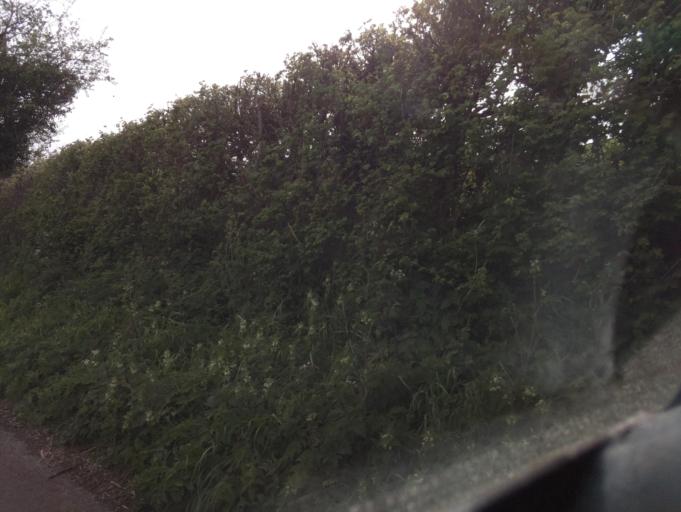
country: GB
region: England
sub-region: Somerset
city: Milborne Port
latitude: 50.9733
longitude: -2.4922
